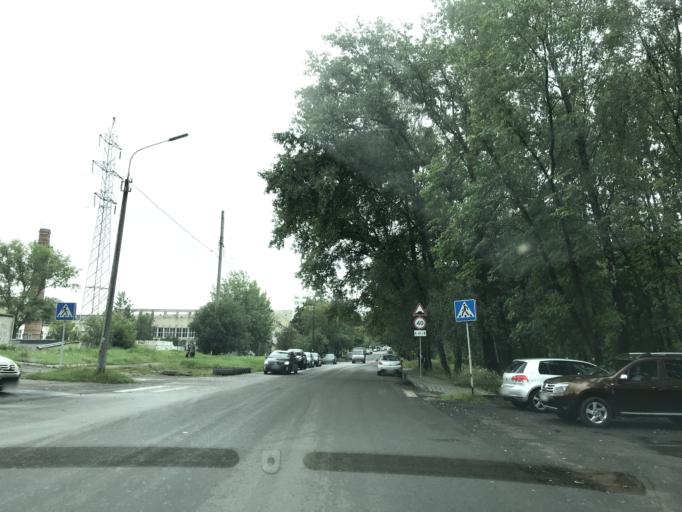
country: BY
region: Minsk
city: Minsk
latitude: 53.9457
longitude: 27.6178
